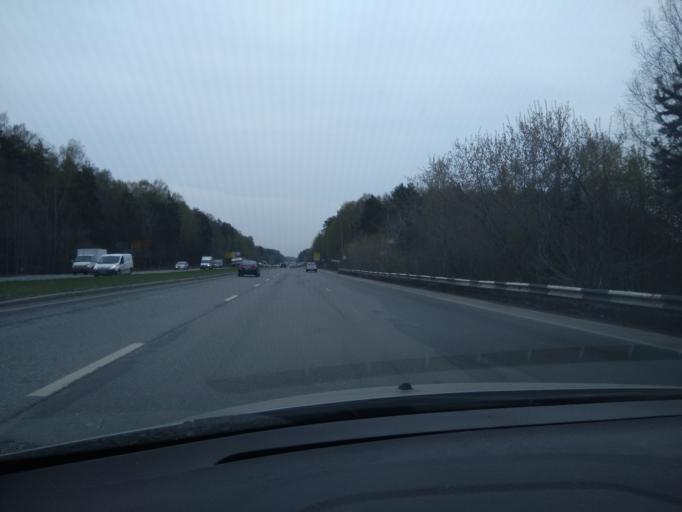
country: RU
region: Sverdlovsk
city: Istok
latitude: 56.8107
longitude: 60.7587
